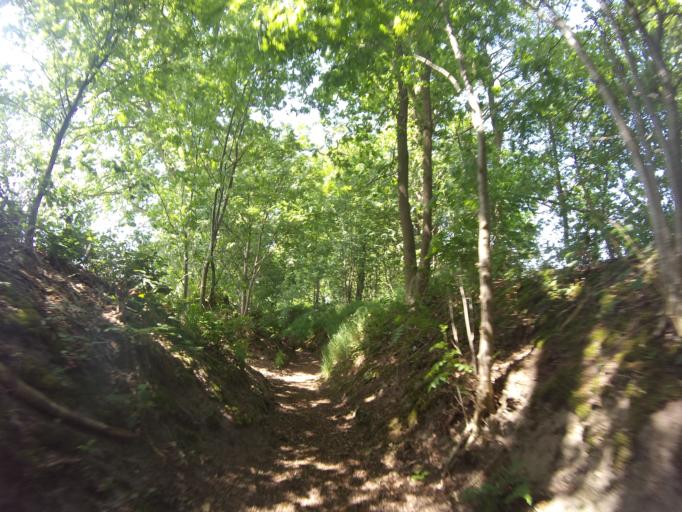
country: NL
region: Utrecht
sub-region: Gemeente Leusden
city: Leusden
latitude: 52.1333
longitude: 5.4597
